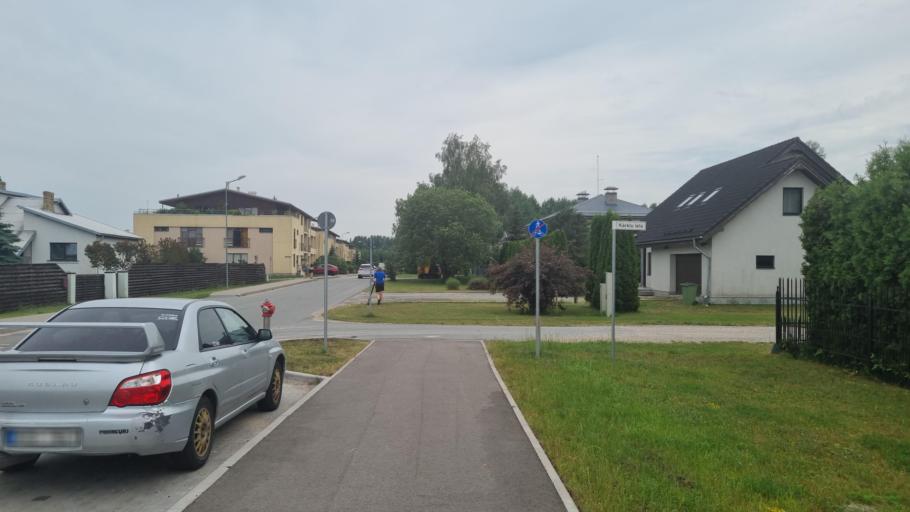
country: LV
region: Kekava
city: Balozi
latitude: 56.8772
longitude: 24.1471
